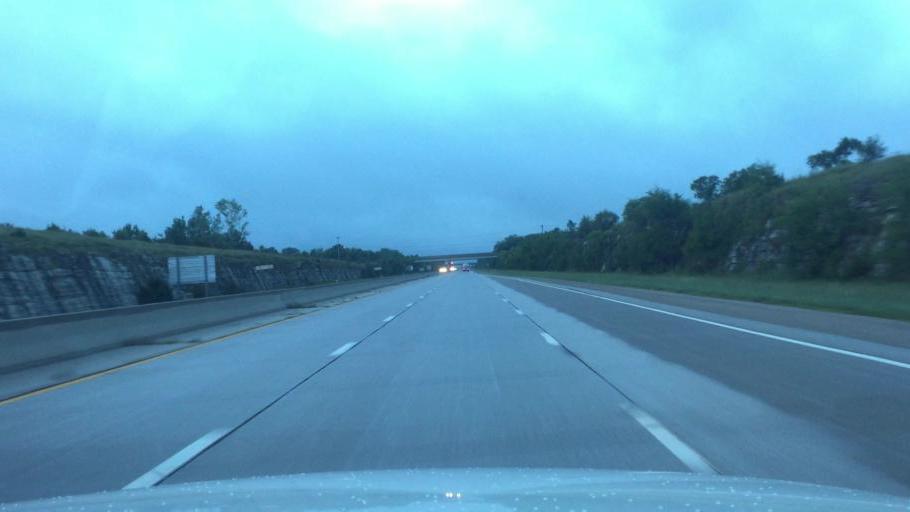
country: US
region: Kansas
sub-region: Neosho County
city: Chanute
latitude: 37.6859
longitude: -95.4796
